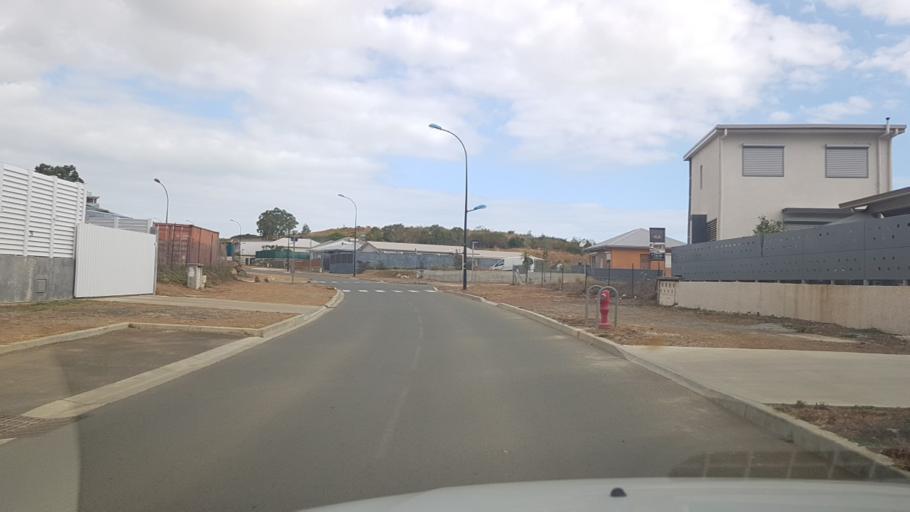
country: NC
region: South Province
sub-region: Dumbea
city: Dumbea
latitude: -22.2017
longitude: 166.4421
